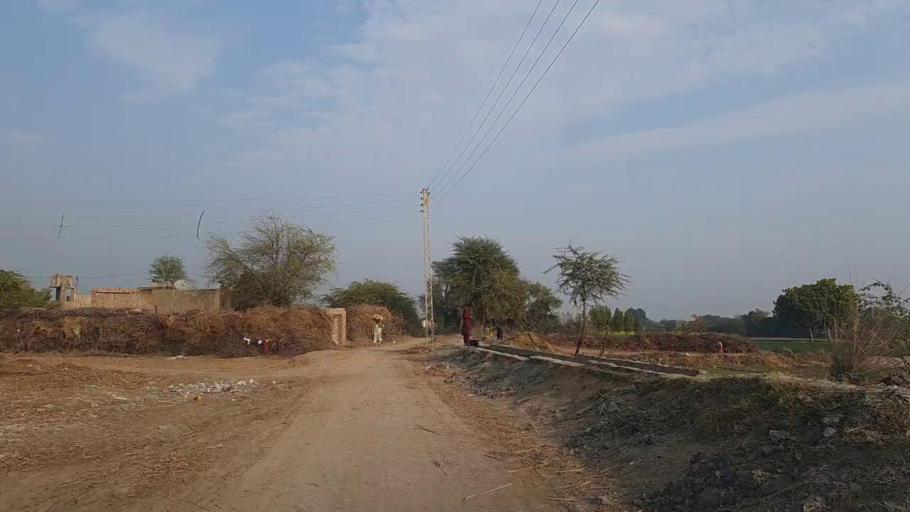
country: PK
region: Sindh
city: Jam Sahib
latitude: 26.3098
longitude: 68.5356
